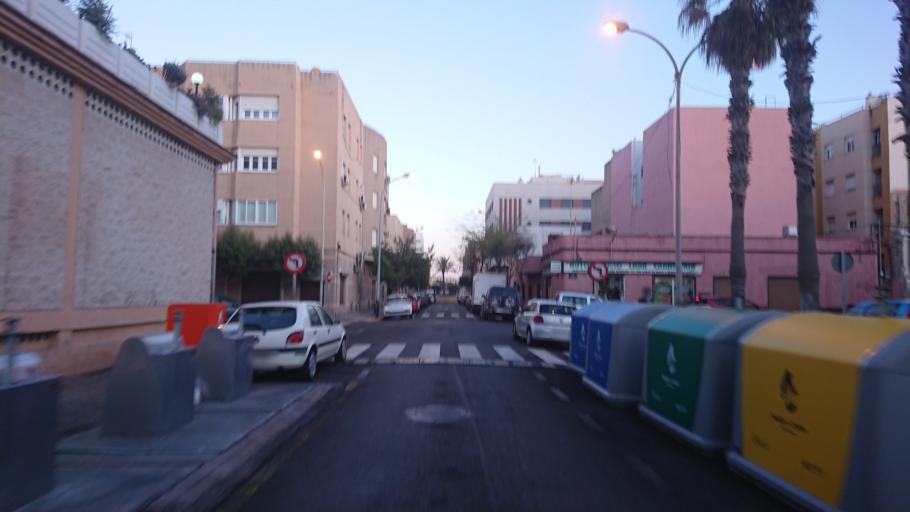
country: ES
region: Melilla
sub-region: Melilla
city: Melilla
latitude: 35.2792
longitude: -2.9371
